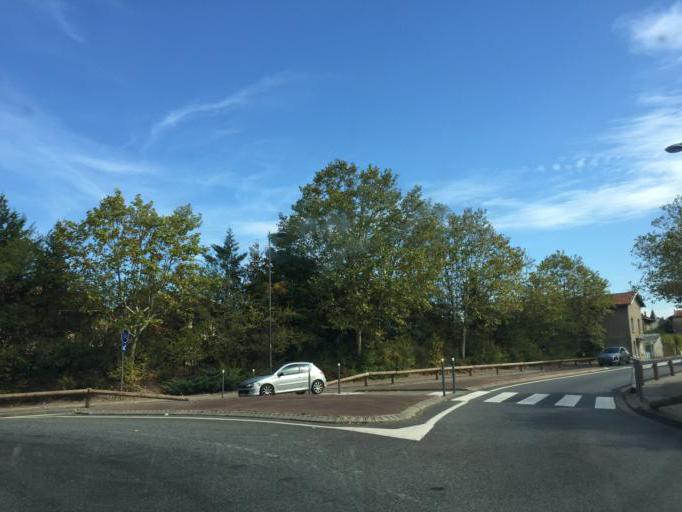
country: FR
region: Rhone-Alpes
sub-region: Departement du Rhone
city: Meyzieu
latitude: 45.7682
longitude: 4.9916
